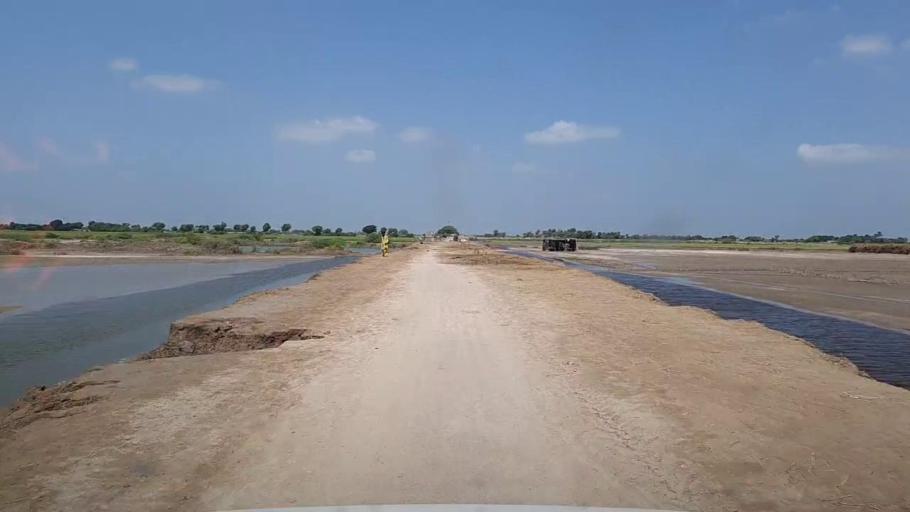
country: PK
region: Sindh
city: Kario
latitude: 24.6970
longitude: 68.5860
